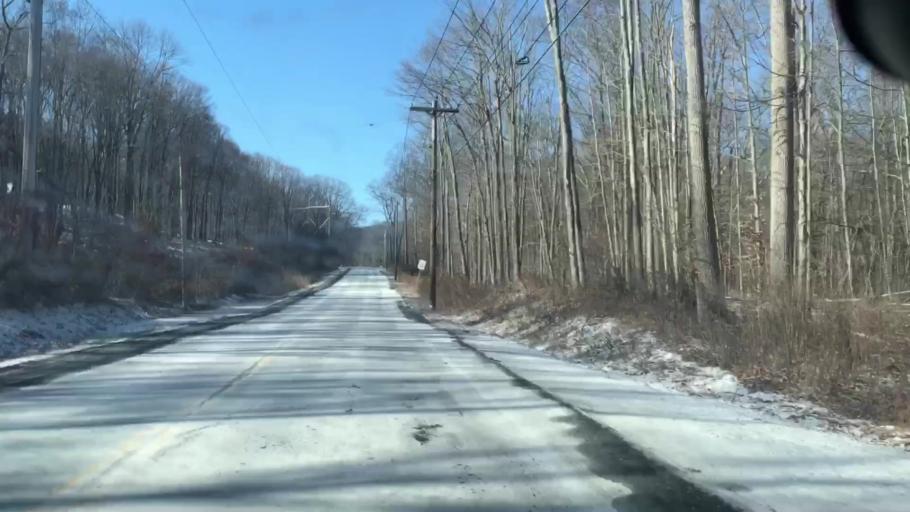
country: US
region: New York
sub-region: Putnam County
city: Carmel Hamlet
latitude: 41.3883
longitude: -73.6838
